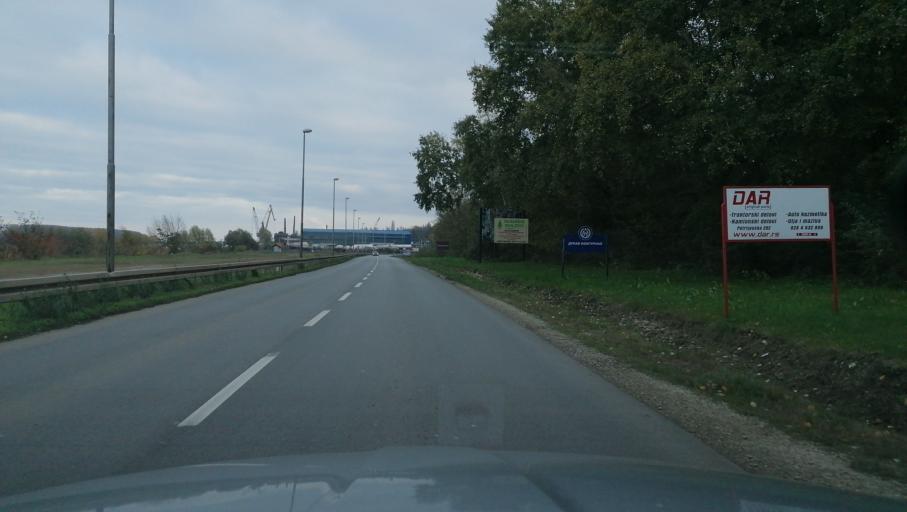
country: RS
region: Central Serbia
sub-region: Podunavski Okrug
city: Smederevo
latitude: 44.6598
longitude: 20.8881
